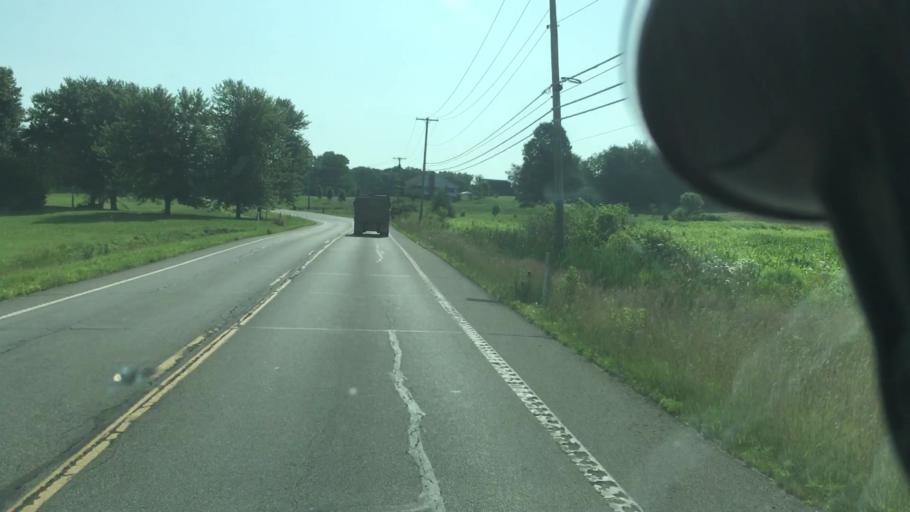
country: US
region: Pennsylvania
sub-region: Lawrence County
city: New Castle
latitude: 41.0140
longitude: -80.2250
